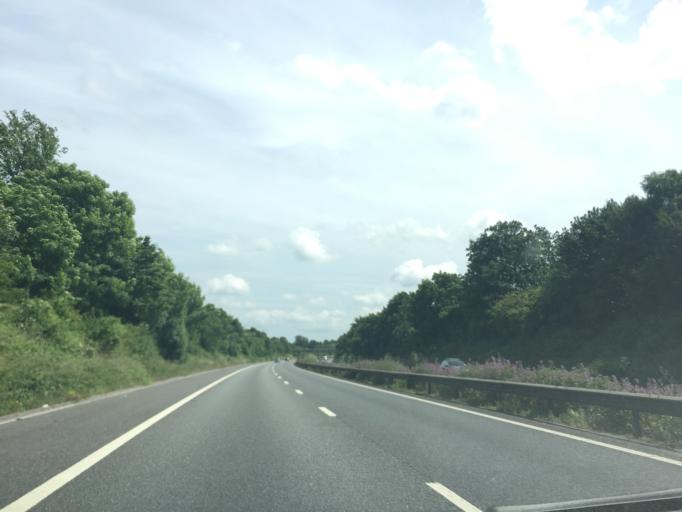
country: GB
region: England
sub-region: Kent
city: Newington
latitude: 51.3199
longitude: 0.6908
